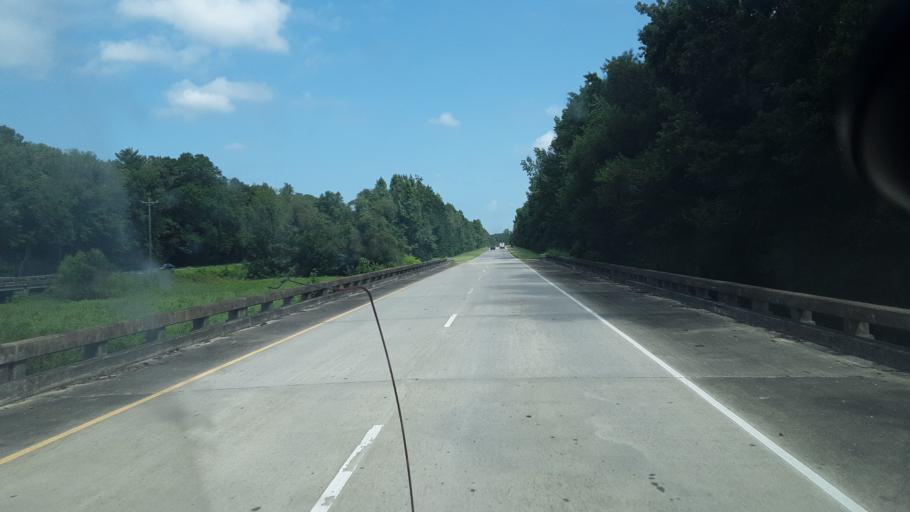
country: US
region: South Carolina
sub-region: Bamberg County
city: Bamberg
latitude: 33.3374
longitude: -81.0182
